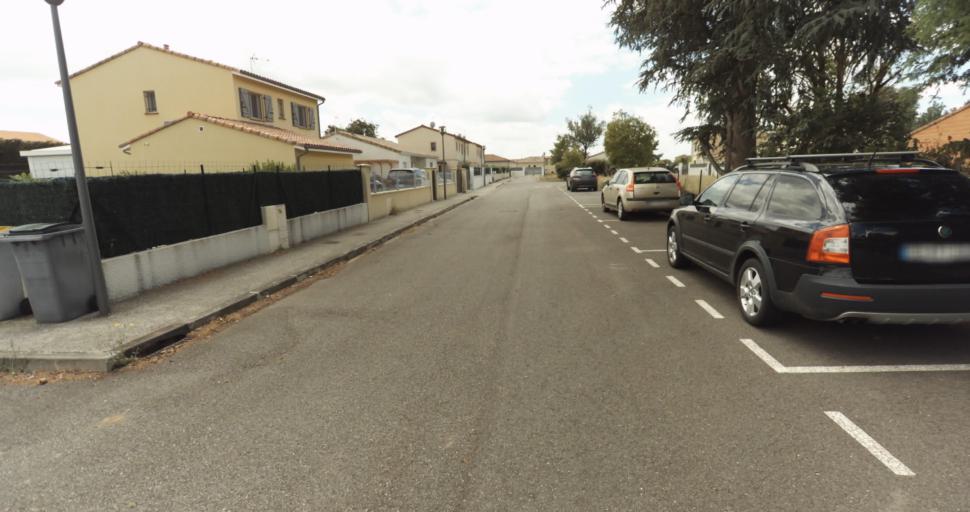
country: FR
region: Midi-Pyrenees
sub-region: Departement de la Haute-Garonne
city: Fontenilles
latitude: 43.5504
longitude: 1.1904
